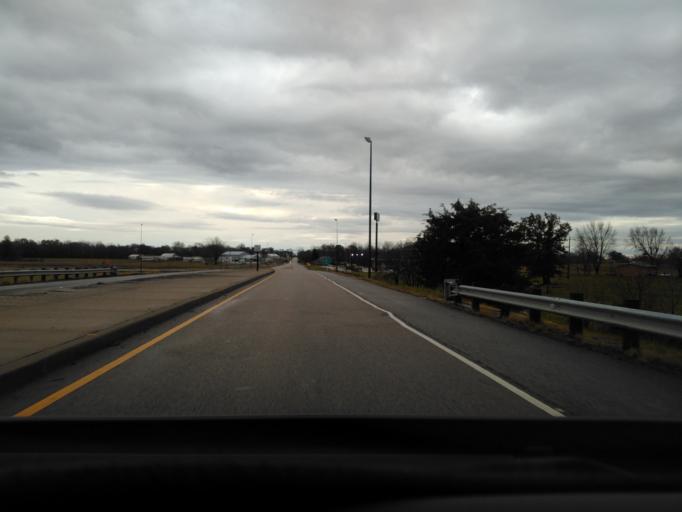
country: US
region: Illinois
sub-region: Bond County
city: Greenville
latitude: 38.8706
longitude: -89.3851
